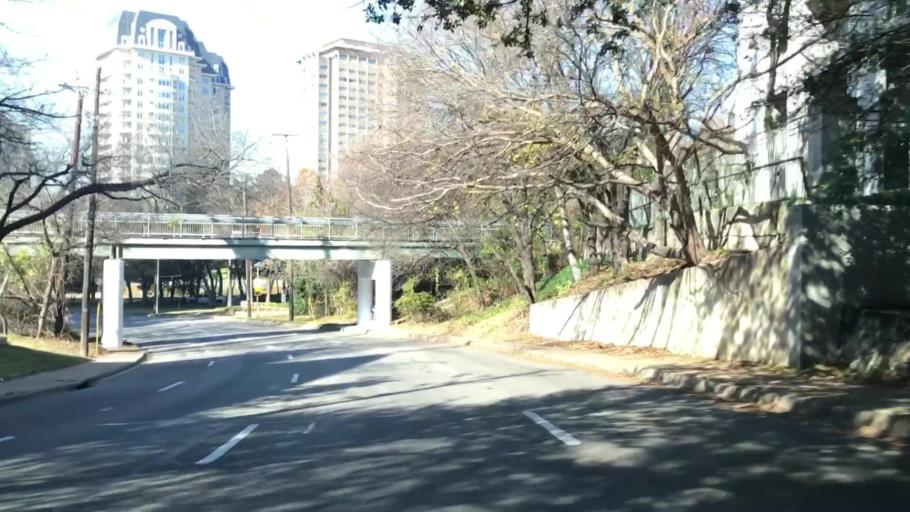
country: US
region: Texas
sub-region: Dallas County
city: Highland Park
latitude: 32.8092
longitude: -96.8003
